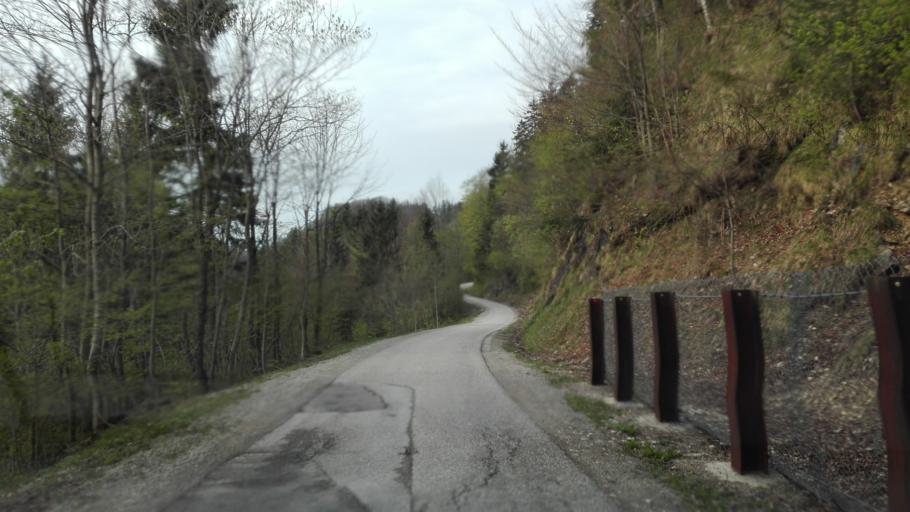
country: AT
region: Upper Austria
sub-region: Politischer Bezirk Steyr-Land
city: Ternberg
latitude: 47.9157
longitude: 14.3506
